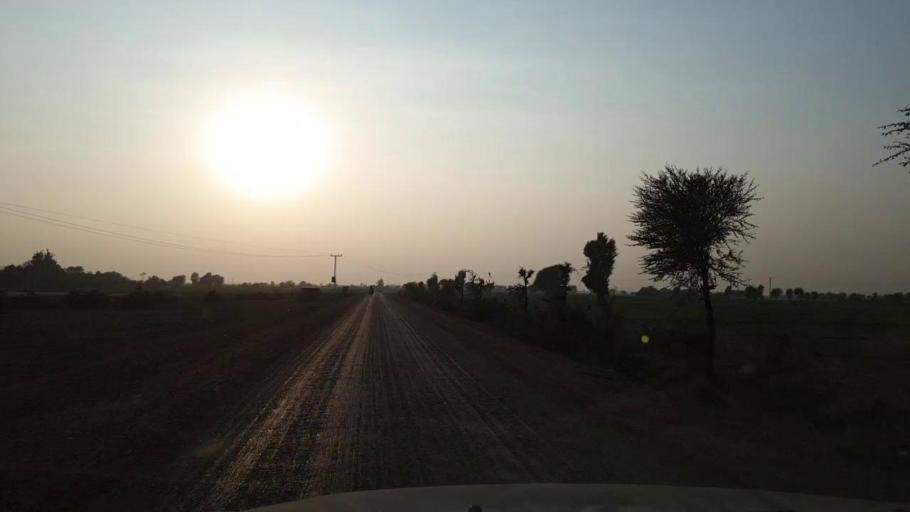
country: PK
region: Sindh
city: Mirpur Khas
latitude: 25.6477
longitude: 69.1779
